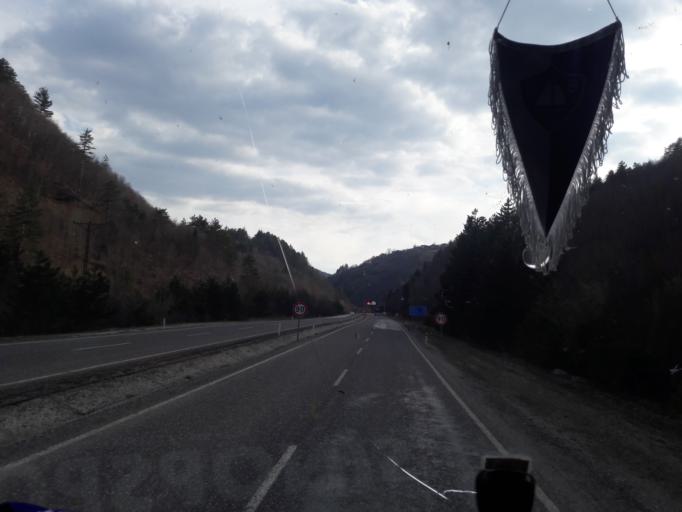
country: TR
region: Kastamonu
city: Kuzyaka
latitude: 41.1471
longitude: 33.7823
